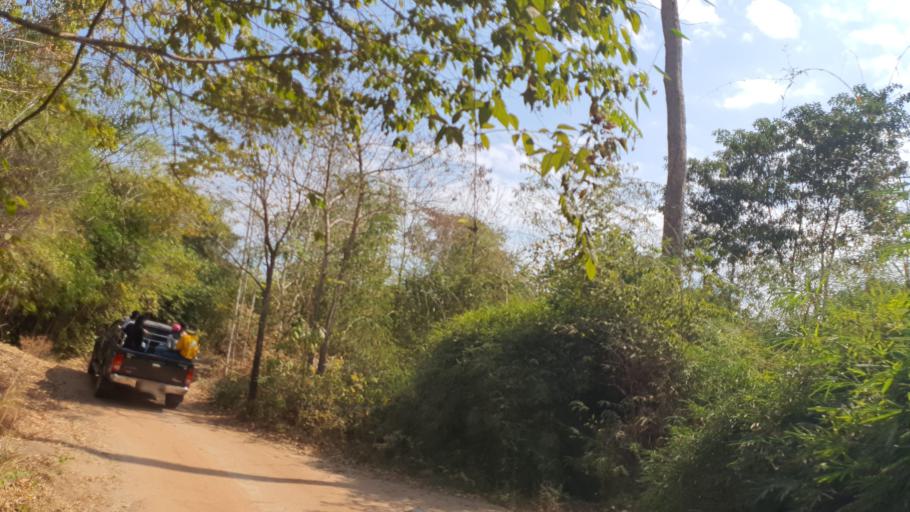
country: TH
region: Changwat Bueng Kan
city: Si Wilai
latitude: 18.2680
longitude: 103.7990
